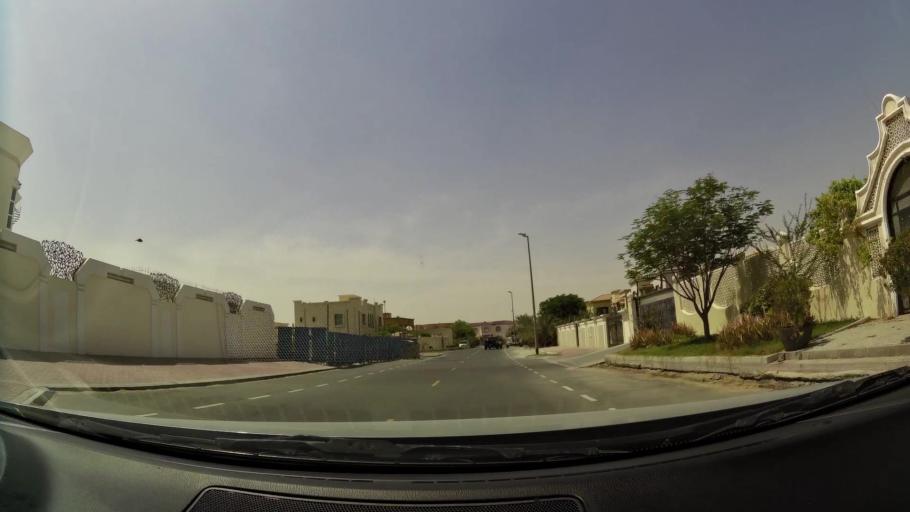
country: AE
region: Ash Shariqah
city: Sharjah
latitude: 25.1830
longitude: 55.4187
